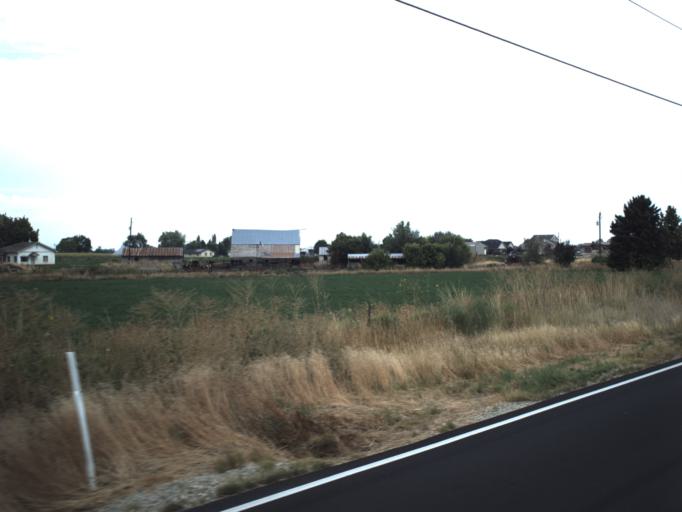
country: US
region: Utah
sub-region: Weber County
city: West Haven
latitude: 41.2349
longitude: -112.0928
